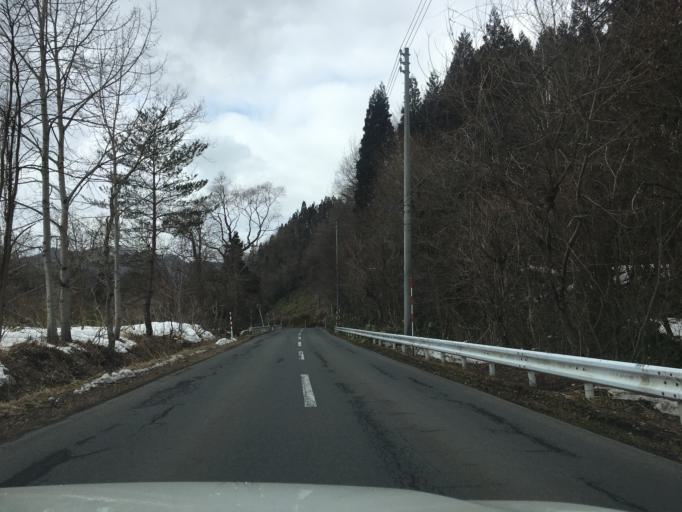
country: JP
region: Akita
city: Odate
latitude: 40.4360
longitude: 140.6415
